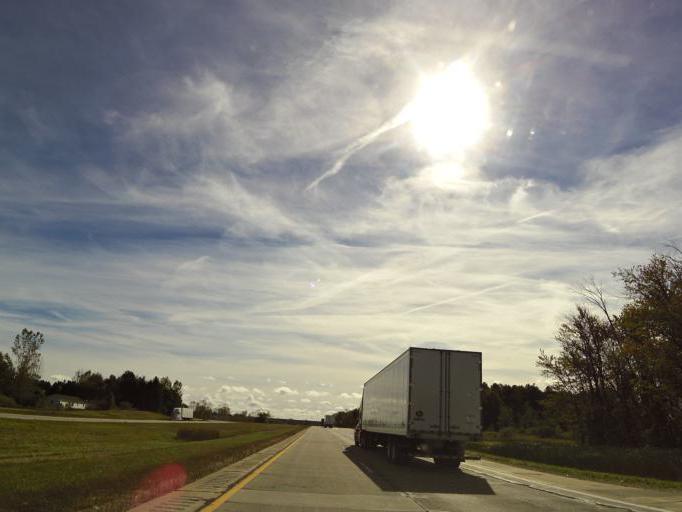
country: US
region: Michigan
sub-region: Saint Clair County
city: Capac
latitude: 42.9840
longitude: -82.8520
